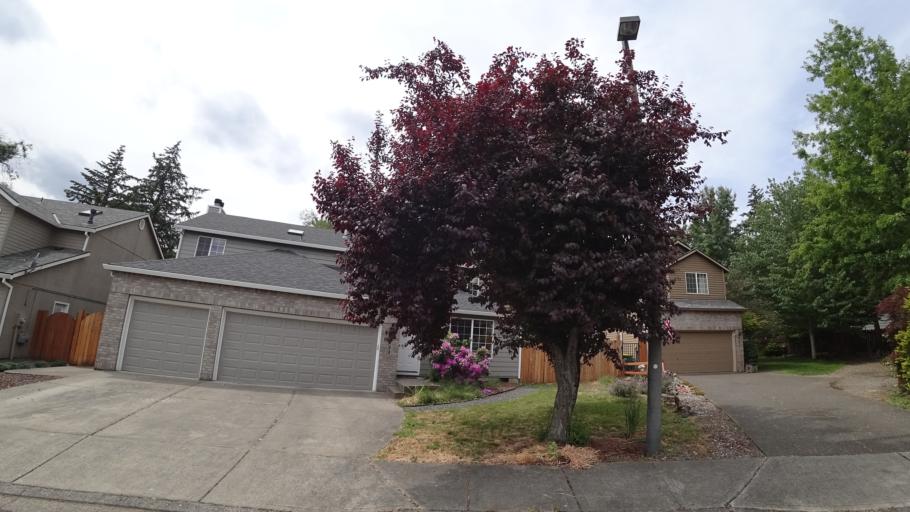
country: US
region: Oregon
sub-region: Washington County
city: Garden Home-Whitford
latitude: 45.4560
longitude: -122.7570
